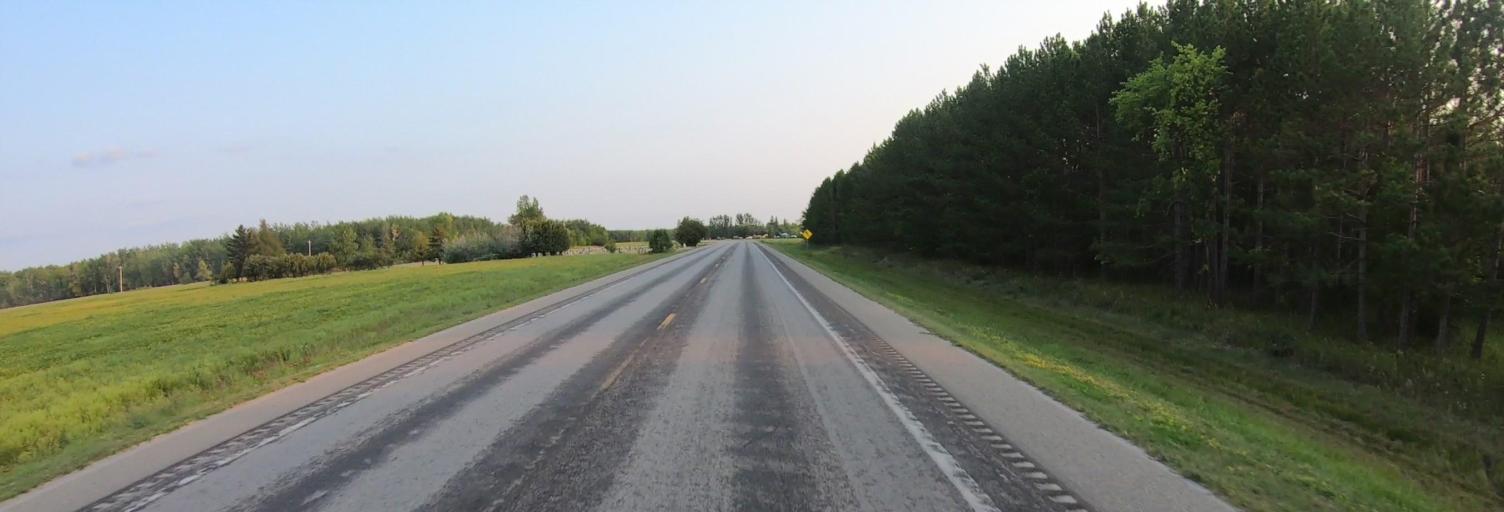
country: US
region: Minnesota
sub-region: Roseau County
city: Warroad
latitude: 48.8892
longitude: -95.3202
